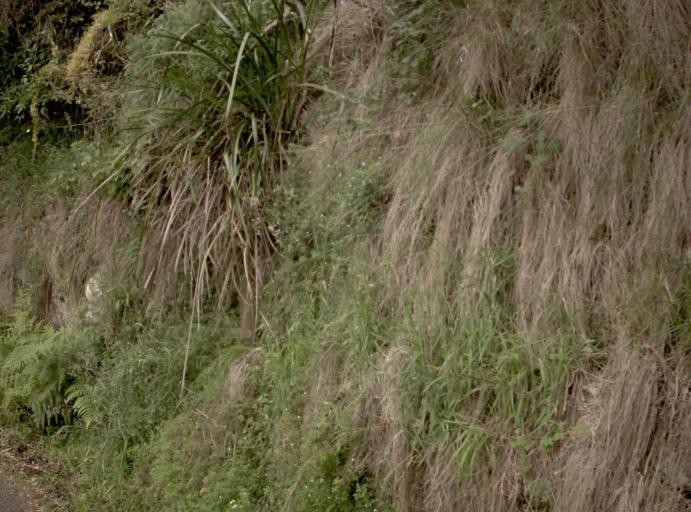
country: AU
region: Victoria
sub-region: Latrobe
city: Traralgon
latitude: -38.4733
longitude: 146.5735
